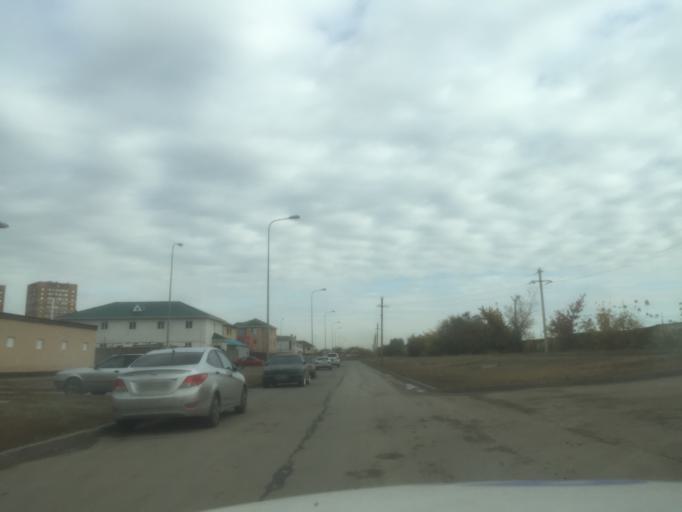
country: KZ
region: Astana Qalasy
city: Astana
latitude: 51.1744
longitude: 71.3752
